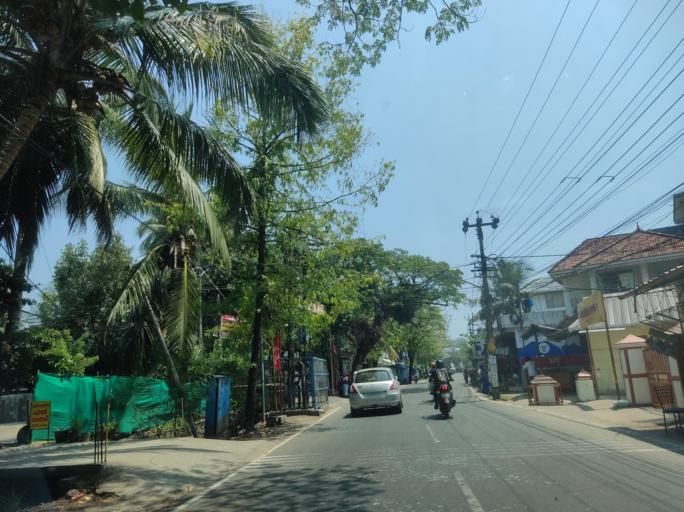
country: IN
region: Kerala
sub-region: Ernakulam
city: Cochin
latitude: 9.9058
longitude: 76.2810
